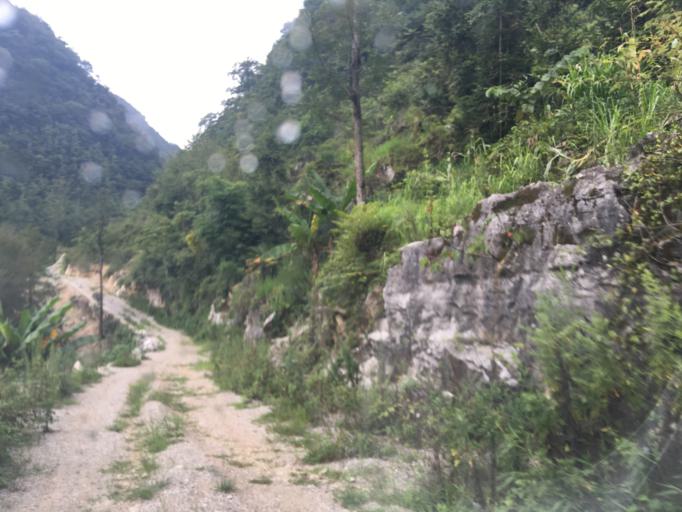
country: CN
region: Guangxi Zhuangzu Zizhiqu
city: Xinzhou
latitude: 25.2240
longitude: 105.6284
